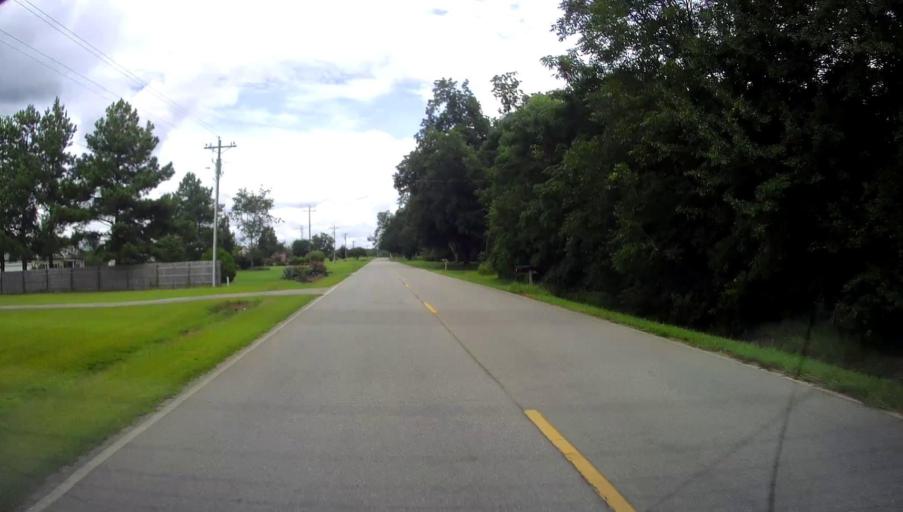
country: US
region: Georgia
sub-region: Peach County
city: Byron
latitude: 32.5600
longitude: -83.7534
